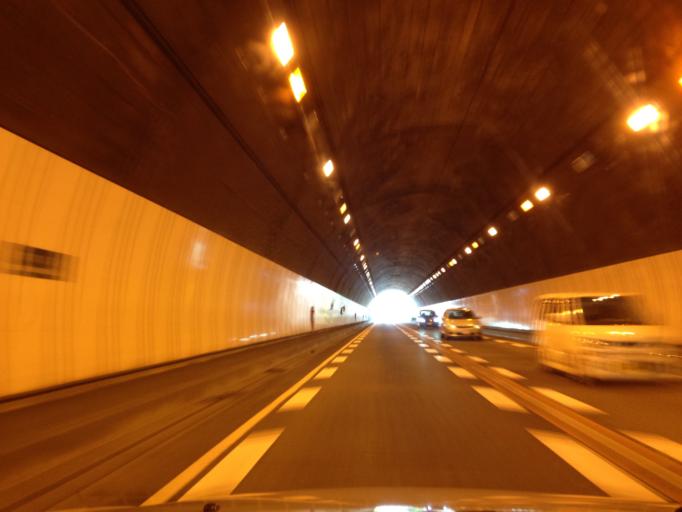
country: JP
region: Shizuoka
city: Kanaya
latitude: 34.7986
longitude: 138.0778
